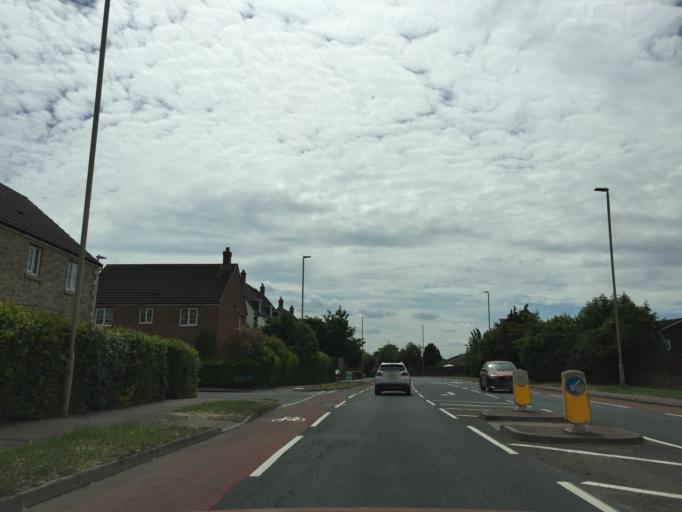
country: GB
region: England
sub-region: Gloucestershire
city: Gloucester
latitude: 51.8242
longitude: -2.2773
